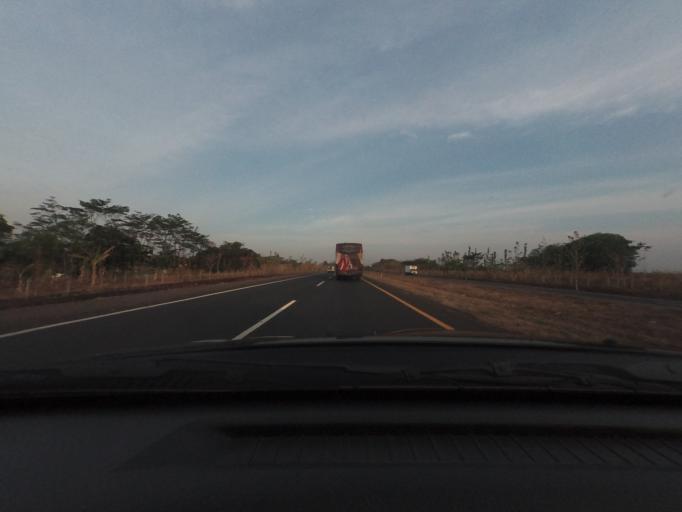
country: ID
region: West Java
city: Pamanukan
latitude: -6.5323
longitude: 107.8248
